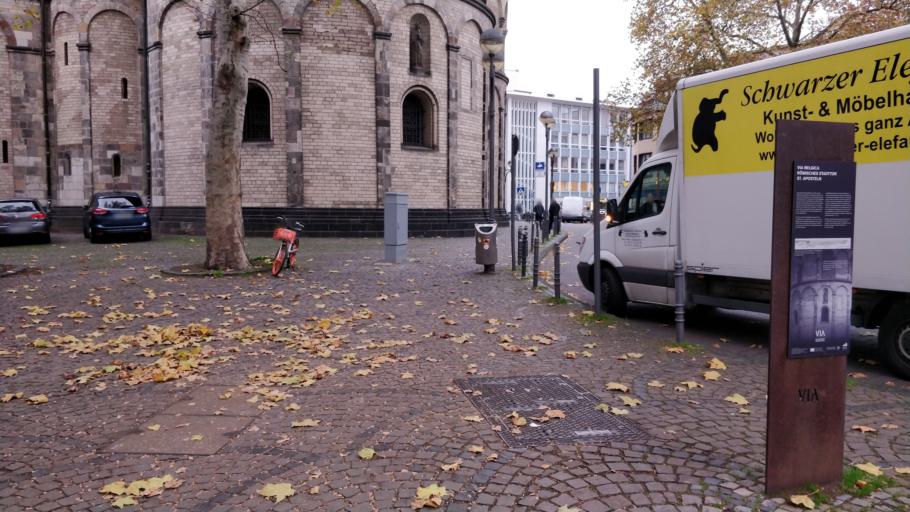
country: DE
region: North Rhine-Westphalia
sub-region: Regierungsbezirk Koln
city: Koeln
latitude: 50.9365
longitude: 6.9459
